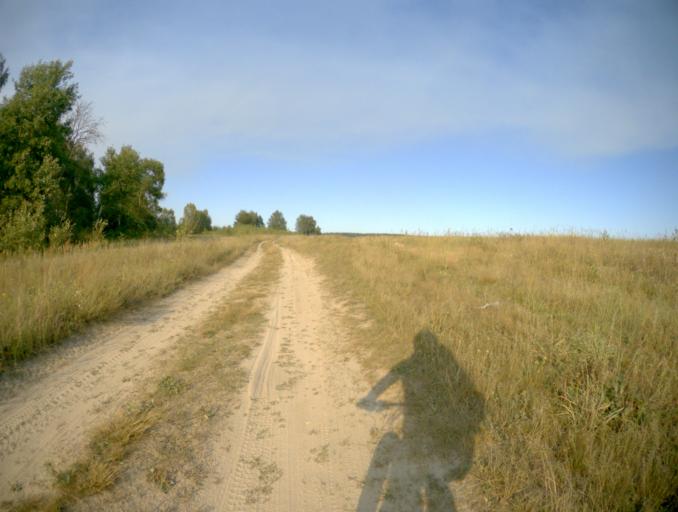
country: RU
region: Vladimir
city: Kosterevo
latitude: 55.9192
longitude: 39.7158
